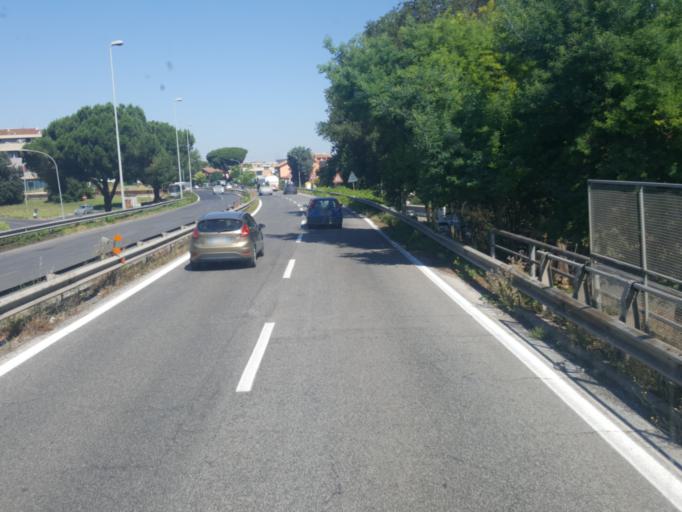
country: IT
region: Latium
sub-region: Citta metropolitana di Roma Capitale
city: Ciampino
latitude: 41.8300
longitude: 12.6206
